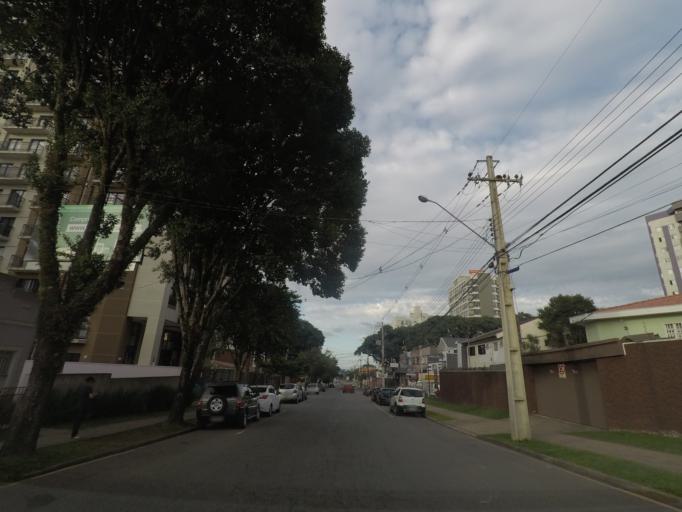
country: BR
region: Parana
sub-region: Curitiba
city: Curitiba
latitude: -25.4751
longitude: -49.2922
